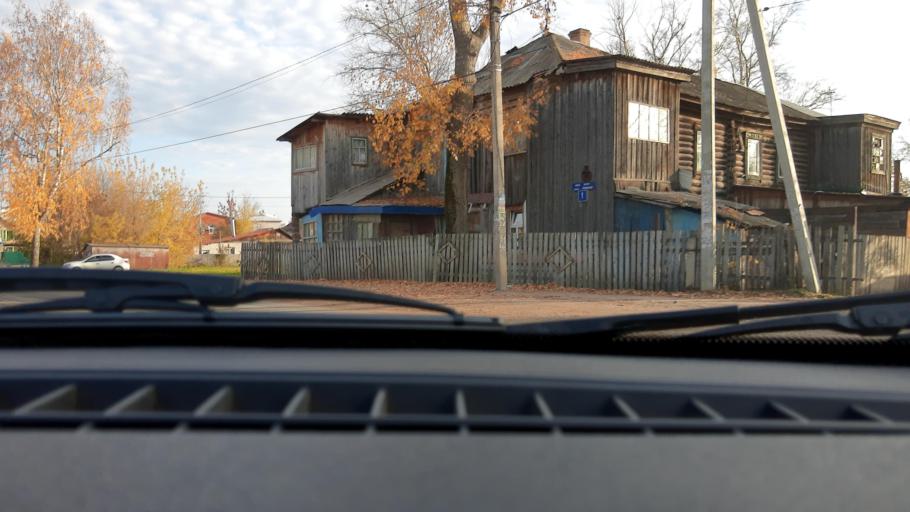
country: RU
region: Bashkortostan
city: Mikhaylovka
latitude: 54.7409
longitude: 55.8983
